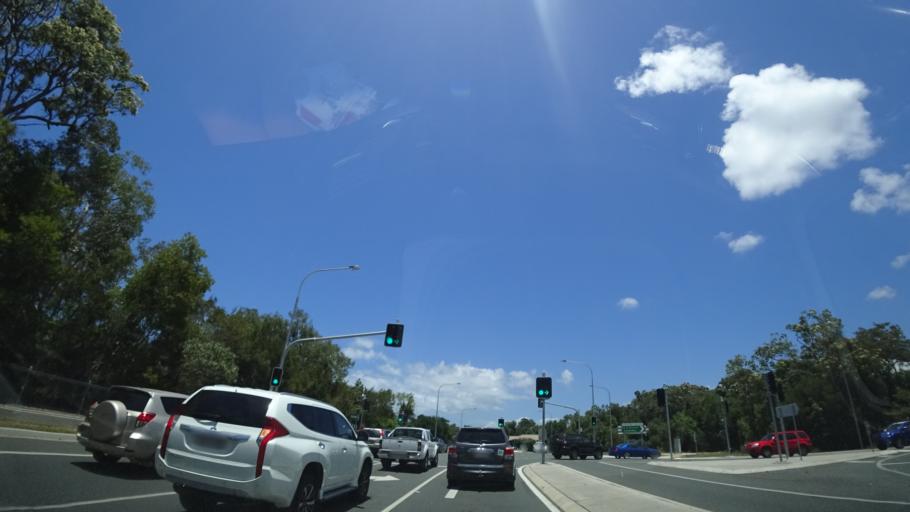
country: AU
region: Queensland
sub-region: Sunshine Coast
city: Little Mountain
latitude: -26.7566
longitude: 153.1117
